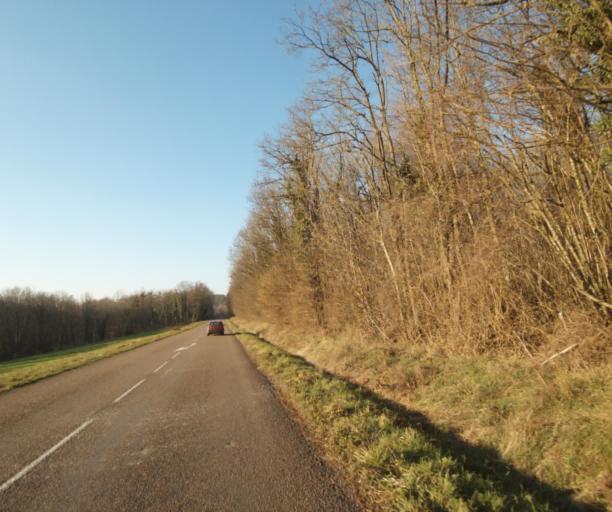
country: FR
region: Champagne-Ardenne
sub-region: Departement de la Haute-Marne
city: Bienville
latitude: 48.5607
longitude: 5.0680
